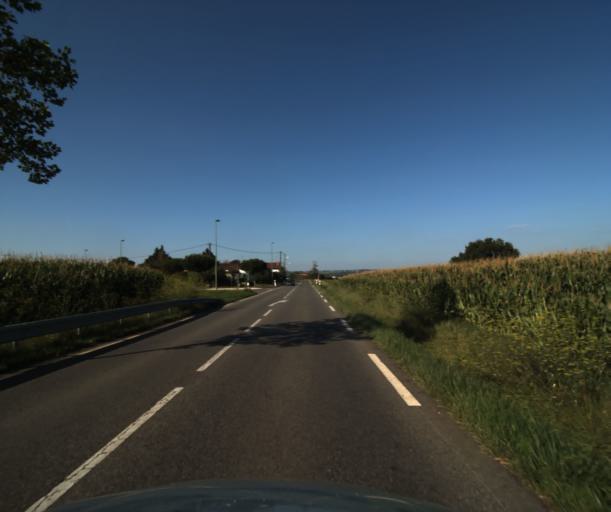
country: FR
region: Midi-Pyrenees
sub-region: Departement de la Haute-Garonne
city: Labarthe-sur-Leze
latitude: 43.4421
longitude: 1.3824
